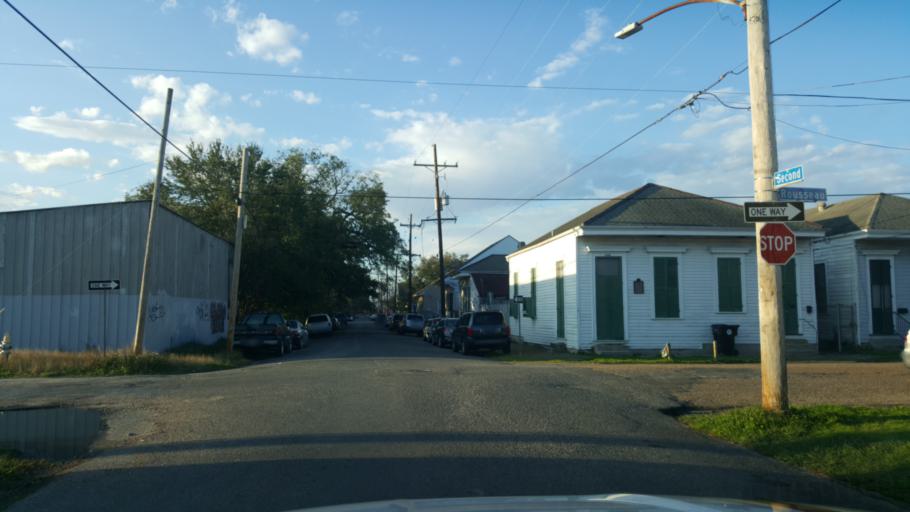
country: US
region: Louisiana
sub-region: Jefferson Parish
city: Harvey
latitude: 29.9222
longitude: -90.0761
